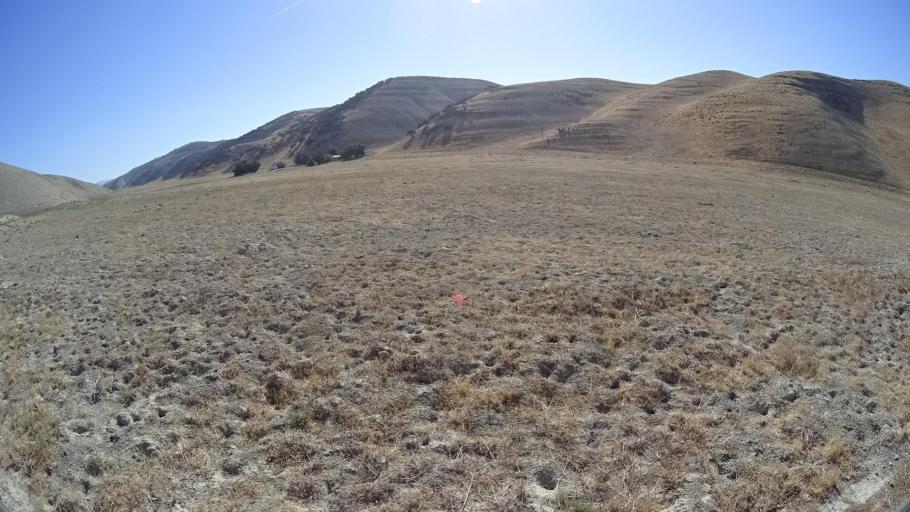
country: US
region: California
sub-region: Monterey County
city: King City
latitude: 36.2007
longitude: -120.9460
